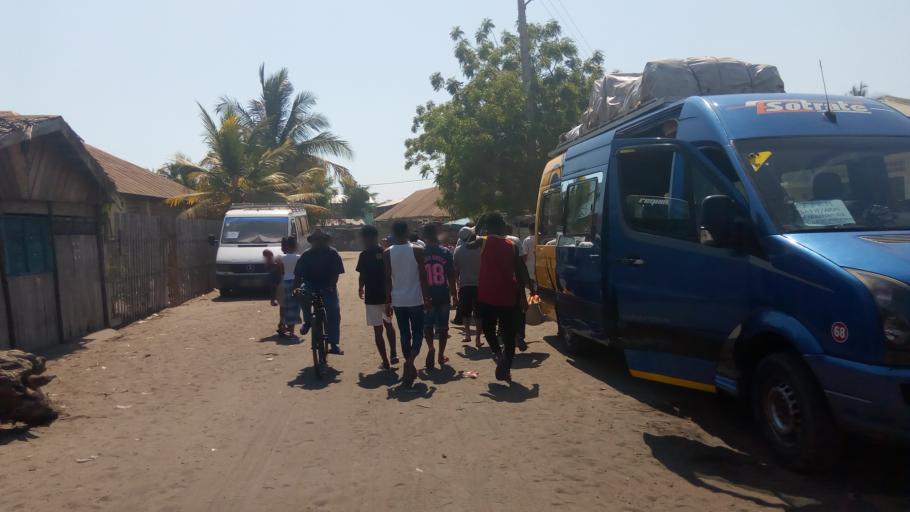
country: MG
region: Menabe
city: Morondava
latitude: -20.2906
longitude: 44.2772
